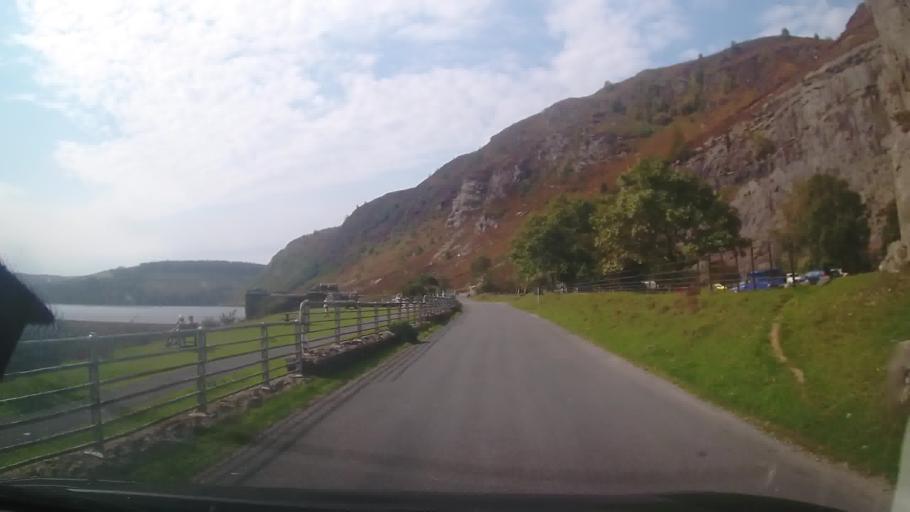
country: GB
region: Wales
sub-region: Sir Powys
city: Rhayader
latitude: 52.2690
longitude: -3.5766
